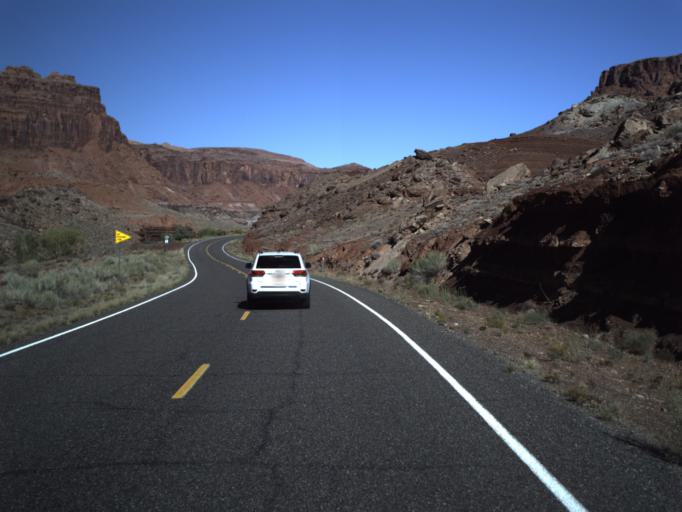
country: US
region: Utah
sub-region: San Juan County
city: Blanding
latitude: 37.8972
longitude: -110.4469
